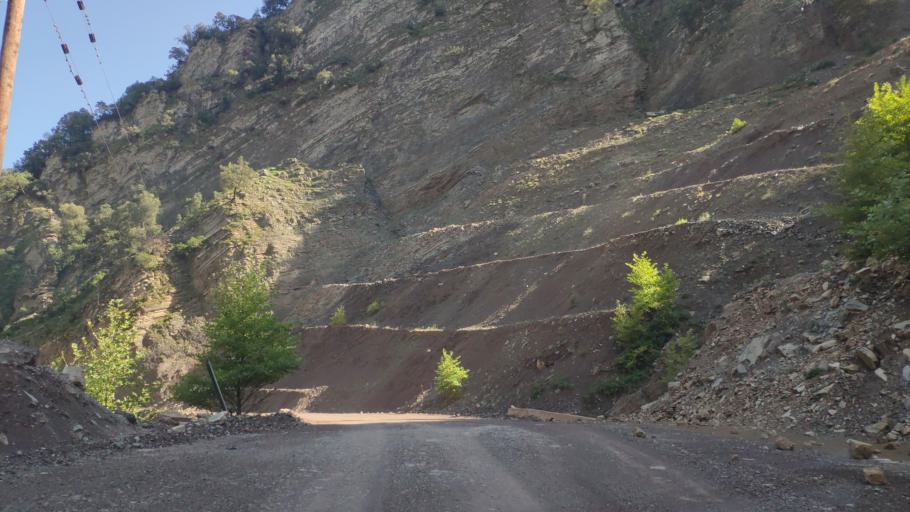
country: GR
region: Central Greece
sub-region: Nomos Evrytanias
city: Kerasochori
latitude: 39.0715
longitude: 21.6017
